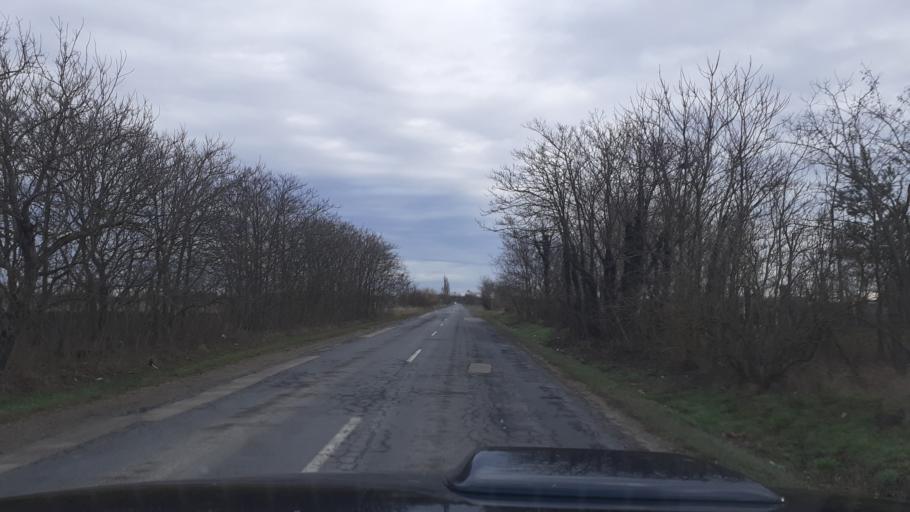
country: HU
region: Fejer
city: Sarosd
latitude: 47.0075
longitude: 18.6919
